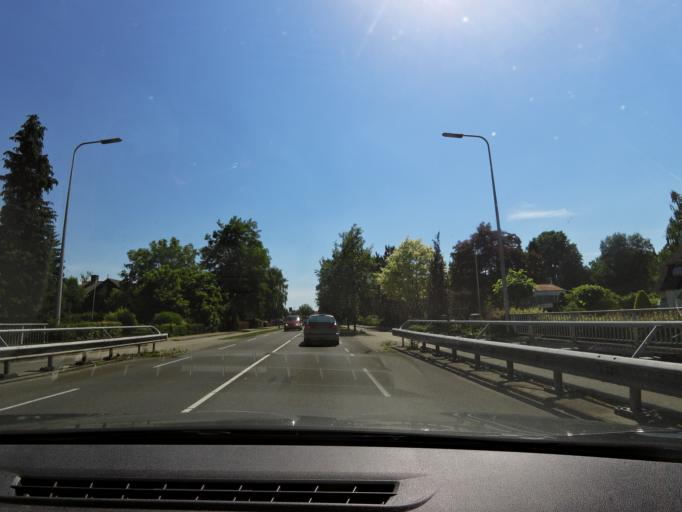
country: NL
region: Gelderland
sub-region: Berkelland
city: Eibergen
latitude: 52.1053
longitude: 6.6521
